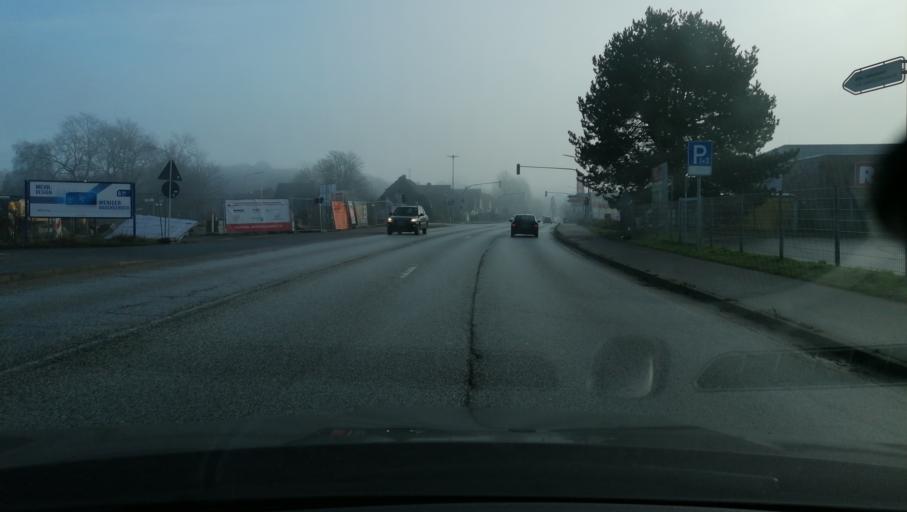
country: DE
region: Schleswig-Holstein
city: Meldorf
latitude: 54.0966
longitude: 9.0641
